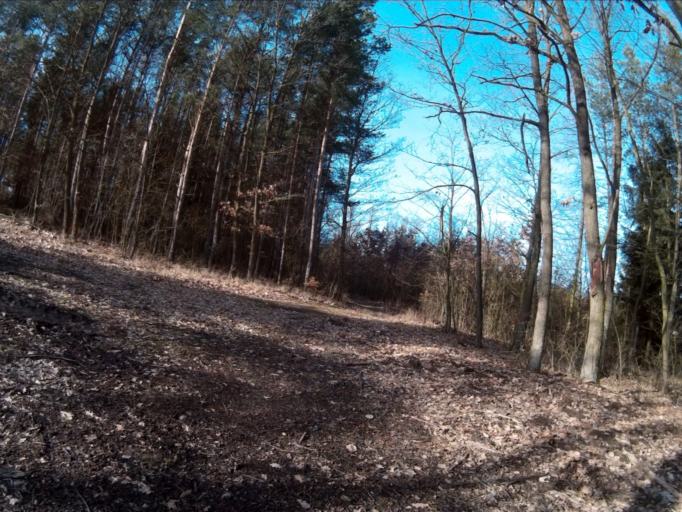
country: CZ
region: Vysocina
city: Mohelno
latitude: 49.1411
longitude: 16.1975
